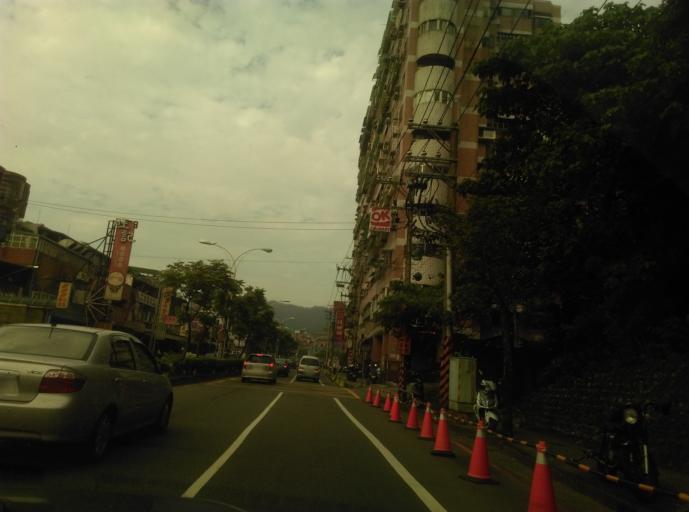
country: TW
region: Taiwan
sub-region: Keelung
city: Keelung
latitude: 25.1534
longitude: 121.6972
